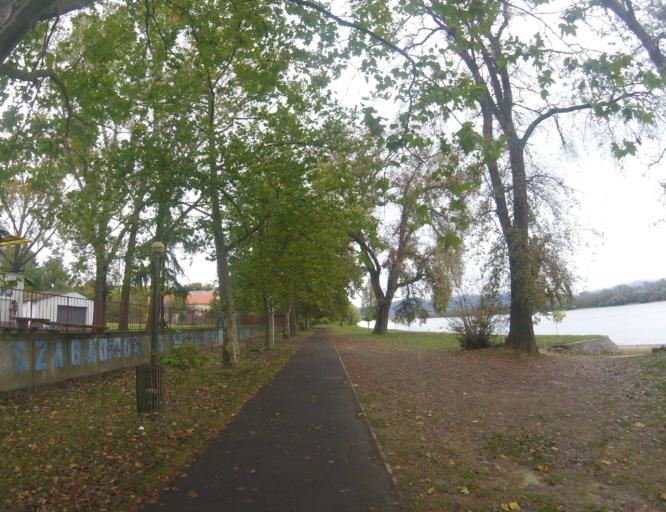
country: HU
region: Pest
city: Szob
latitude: 47.8156
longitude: 18.8635
